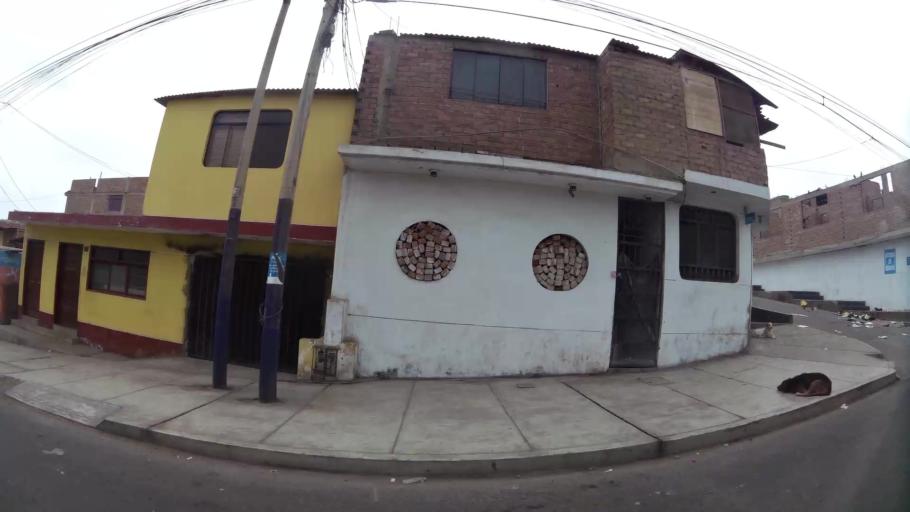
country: PE
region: Lima
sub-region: Lima
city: Surco
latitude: -12.1908
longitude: -76.9908
